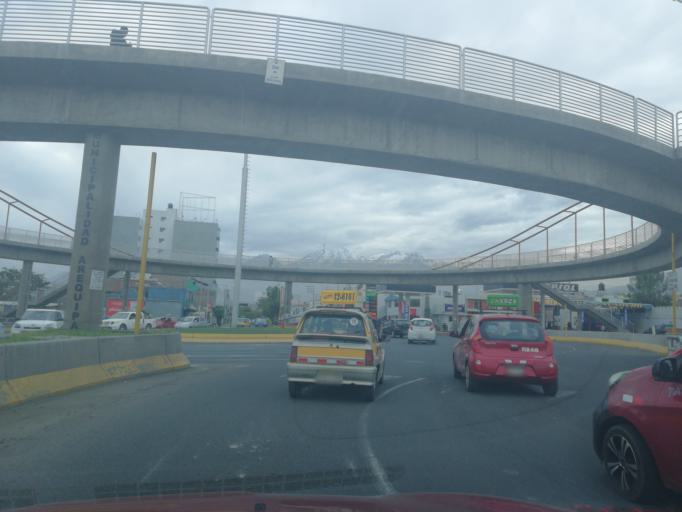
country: PE
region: Arequipa
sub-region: Provincia de Arequipa
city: Arequipa
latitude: -16.4257
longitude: -71.5244
